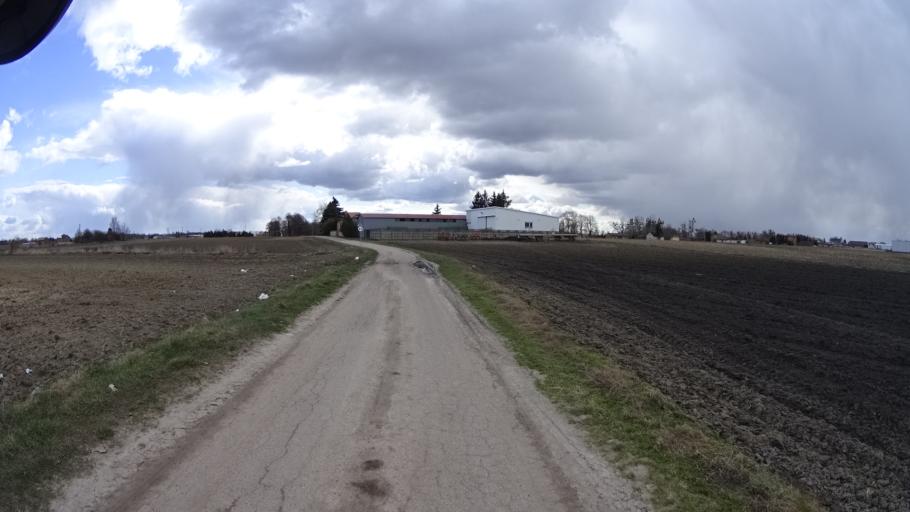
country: PL
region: Masovian Voivodeship
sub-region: Powiat warszawski zachodni
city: Jozefow
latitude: 52.2222
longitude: 20.6773
